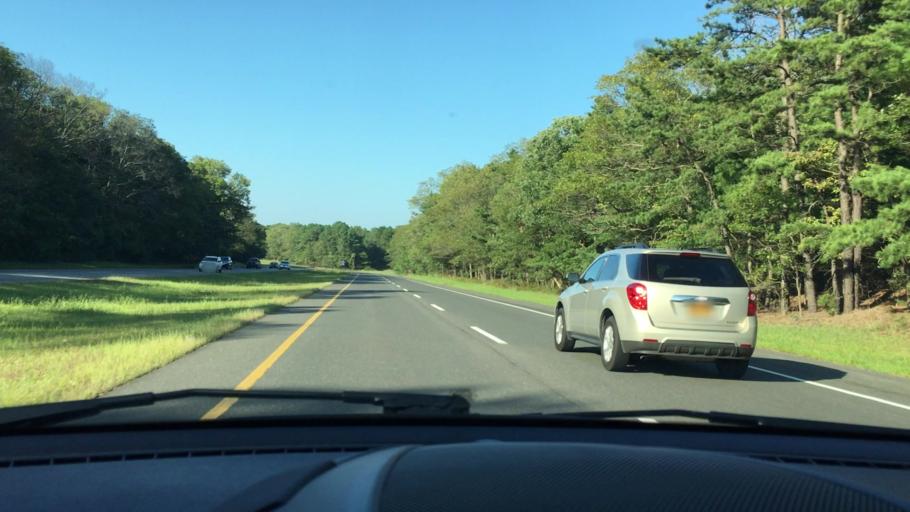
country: US
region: New York
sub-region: Suffolk County
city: Ridge
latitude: 40.8858
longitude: -72.8869
